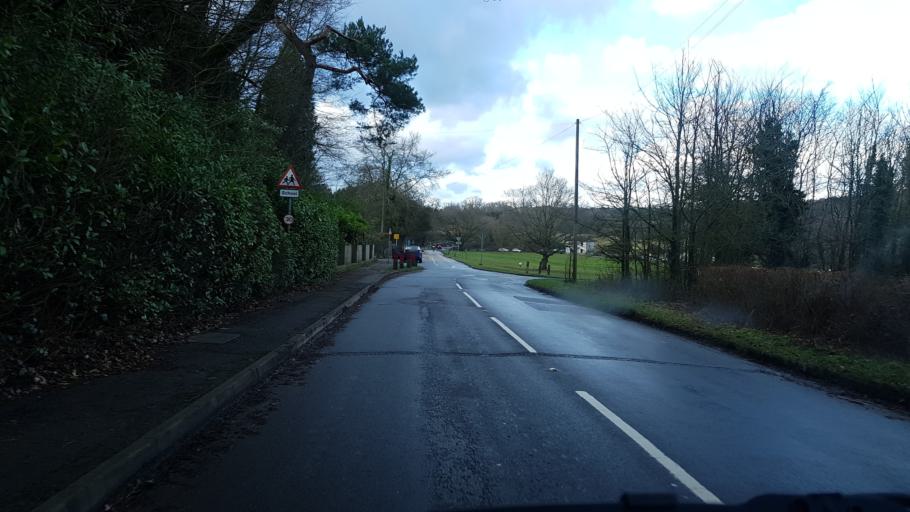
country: GB
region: England
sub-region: Surrey
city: Elstead
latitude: 51.1816
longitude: -0.7523
